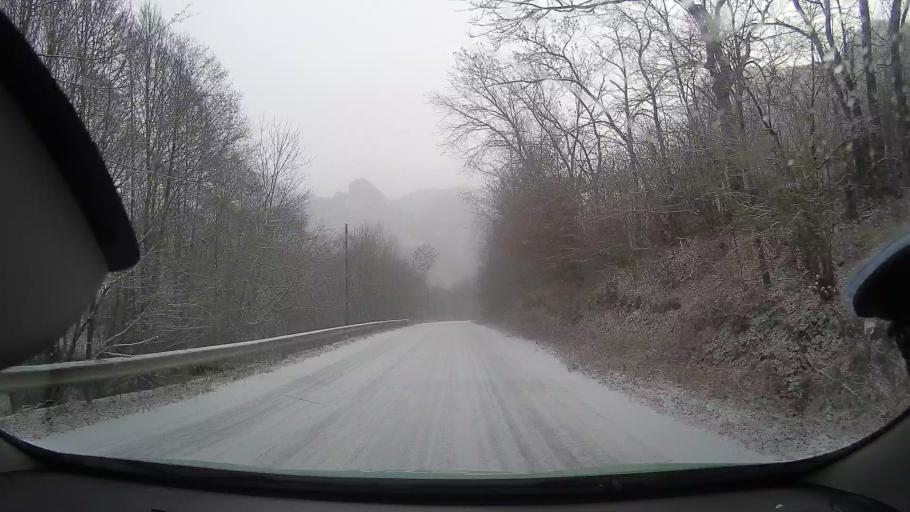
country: RO
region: Alba
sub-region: Comuna Rimetea
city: Rimetea
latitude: 46.3854
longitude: 23.5764
